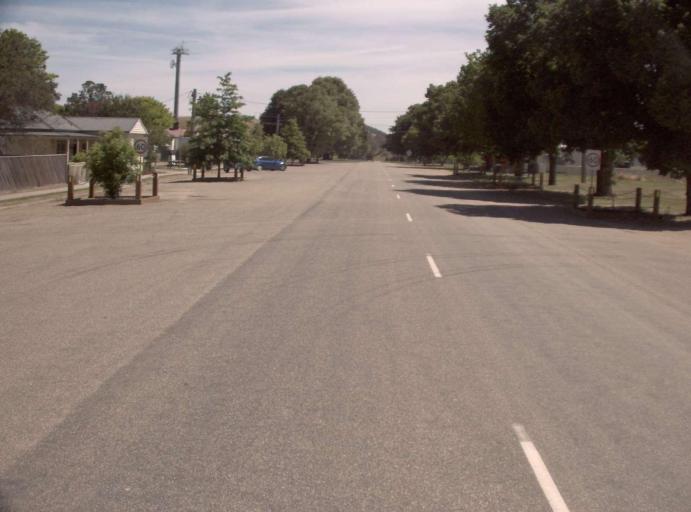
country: AU
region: Victoria
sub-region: Alpine
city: Mount Beauty
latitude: -36.9550
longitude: 147.7032
